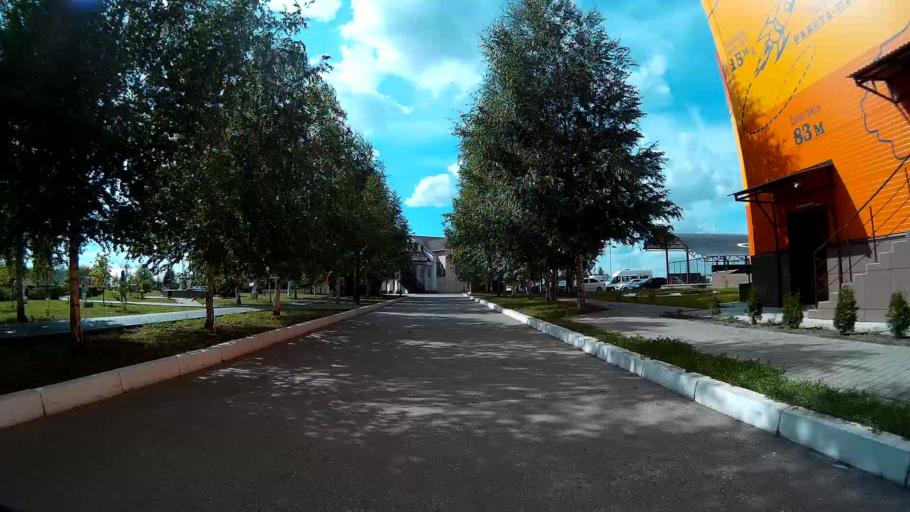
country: RU
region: Ulyanovsk
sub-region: Ulyanovskiy Rayon
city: Ulyanovsk
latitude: 54.2747
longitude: 48.2673
